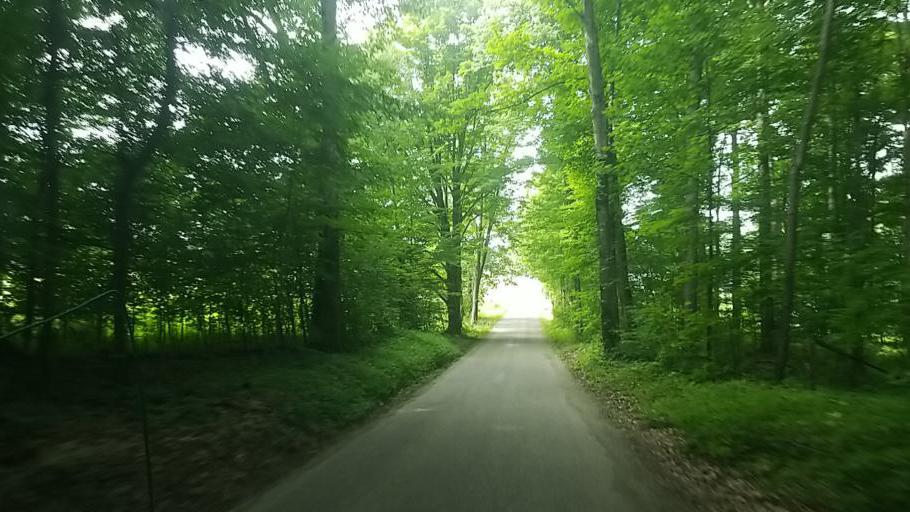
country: US
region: Ohio
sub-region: Richland County
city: Lexington
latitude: 40.6279
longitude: -82.5778
